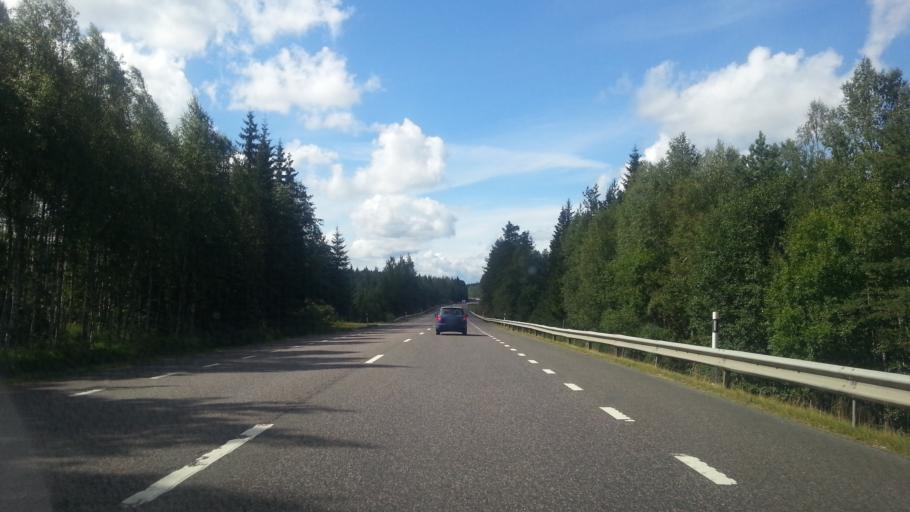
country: SE
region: Dalarna
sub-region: Ludvika Kommun
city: Grangesberg
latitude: 60.0926
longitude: 15.0614
